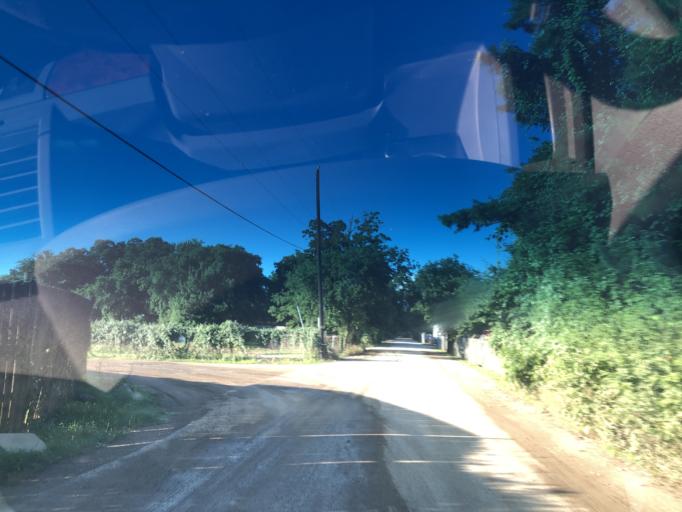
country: US
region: Texas
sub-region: Dallas County
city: Grand Prairie
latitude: 32.7902
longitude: -97.0091
